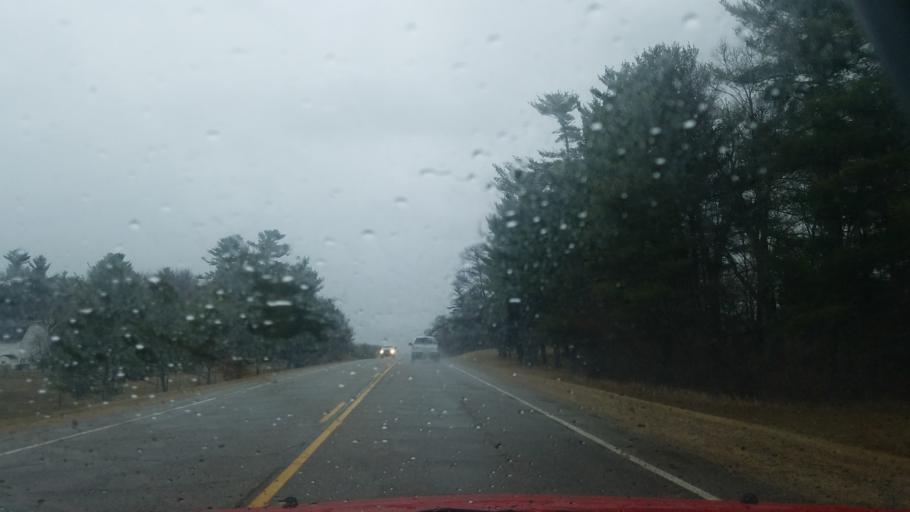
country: US
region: Wisconsin
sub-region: Dunn County
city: Tainter Lake
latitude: 44.9734
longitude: -91.8943
